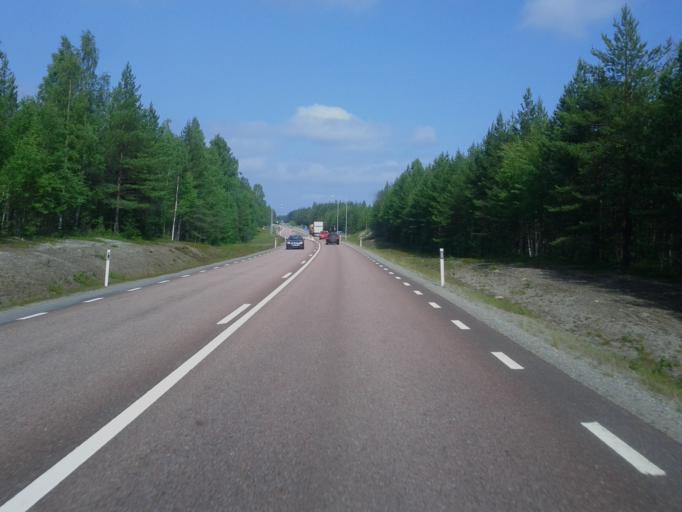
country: SE
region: Vaesterbotten
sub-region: Skelleftea Kommun
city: Burea
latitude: 64.6292
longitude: 21.1772
